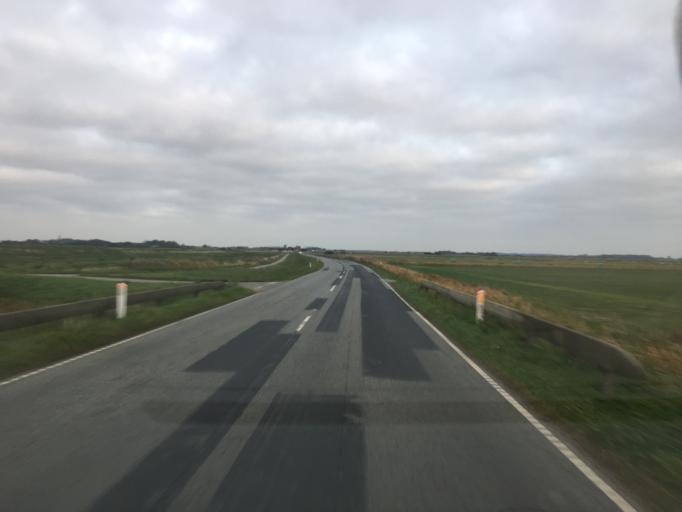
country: DE
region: Schleswig-Holstein
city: Rodenas
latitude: 54.9629
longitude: 8.7166
